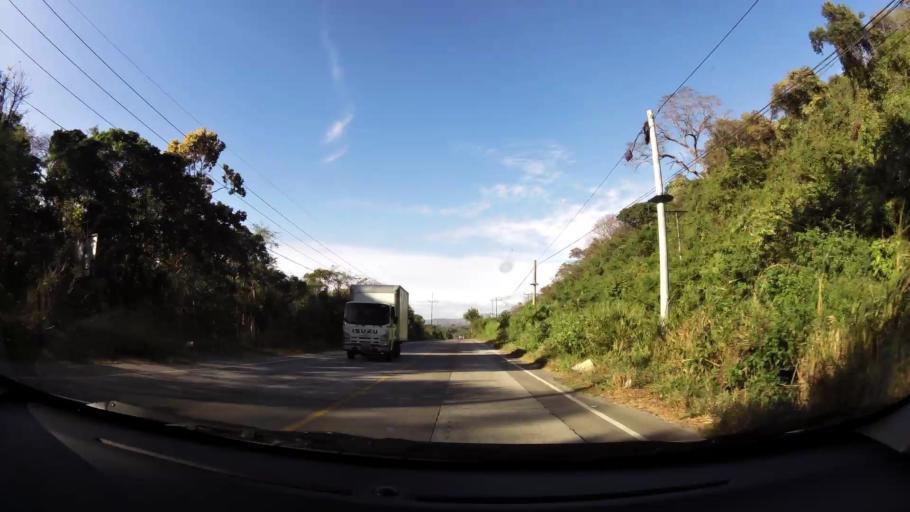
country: SV
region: Santa Ana
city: Metapan
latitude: 14.2681
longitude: -89.4605
